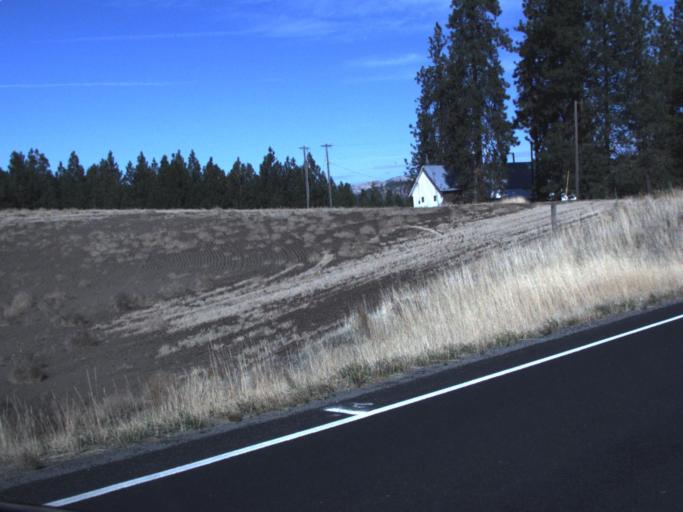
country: US
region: Washington
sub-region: Lincoln County
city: Davenport
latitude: 48.0125
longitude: -118.2485
